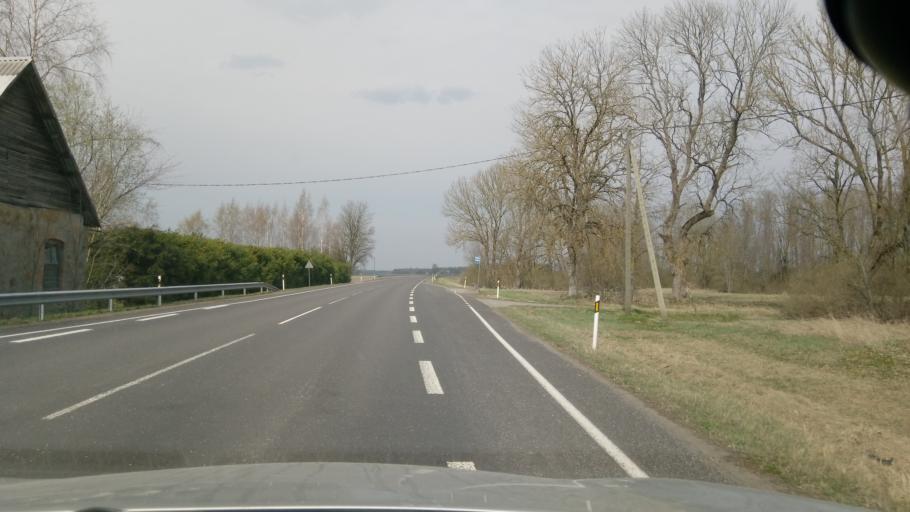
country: EE
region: Viljandimaa
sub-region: Vohma linn
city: Vohma
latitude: 58.6751
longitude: 25.6052
